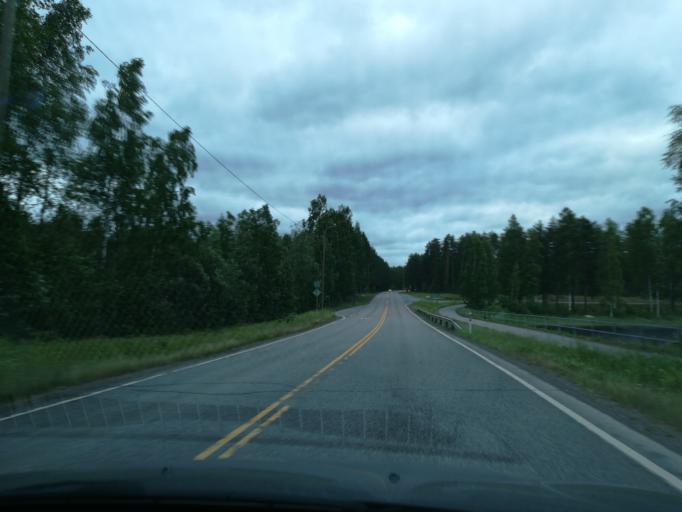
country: FI
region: Southern Savonia
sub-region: Mikkeli
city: Ristiina
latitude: 61.3559
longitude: 27.4006
